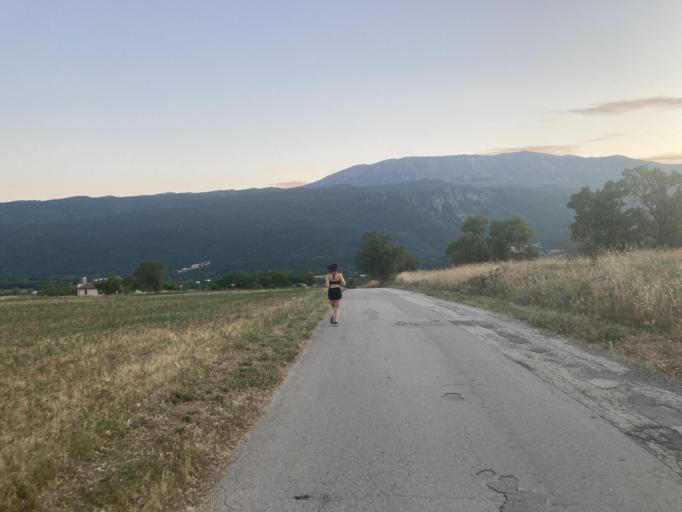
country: IT
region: Abruzzo
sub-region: Provincia dell' Aquila
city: San Demetrio Ne' Vestini
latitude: 42.2946
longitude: 13.5530
